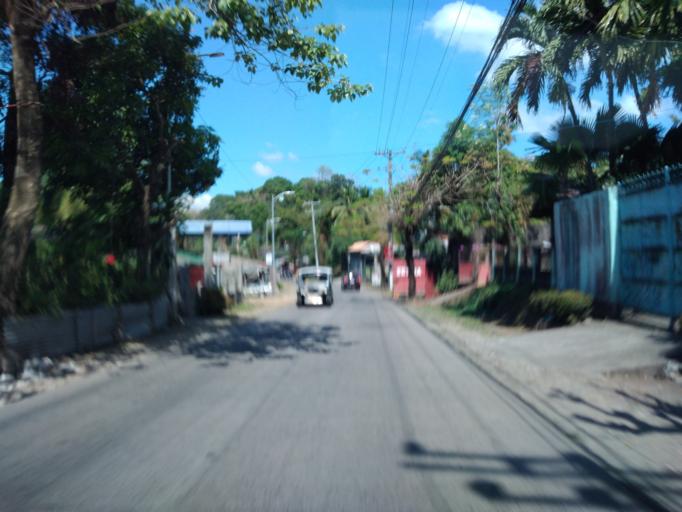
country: PH
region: Central Luzon
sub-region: Province of Bulacan
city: Bitungol
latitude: 14.8573
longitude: 121.0716
